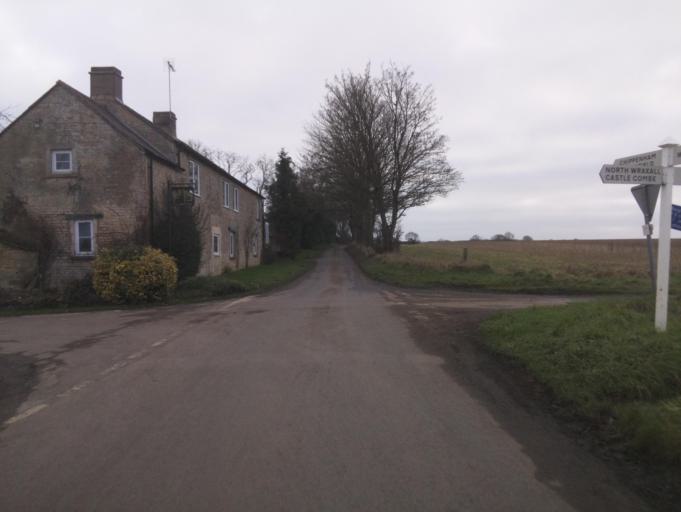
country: GB
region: England
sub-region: Wiltshire
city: Nettleton
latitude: 51.4799
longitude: -2.2860
